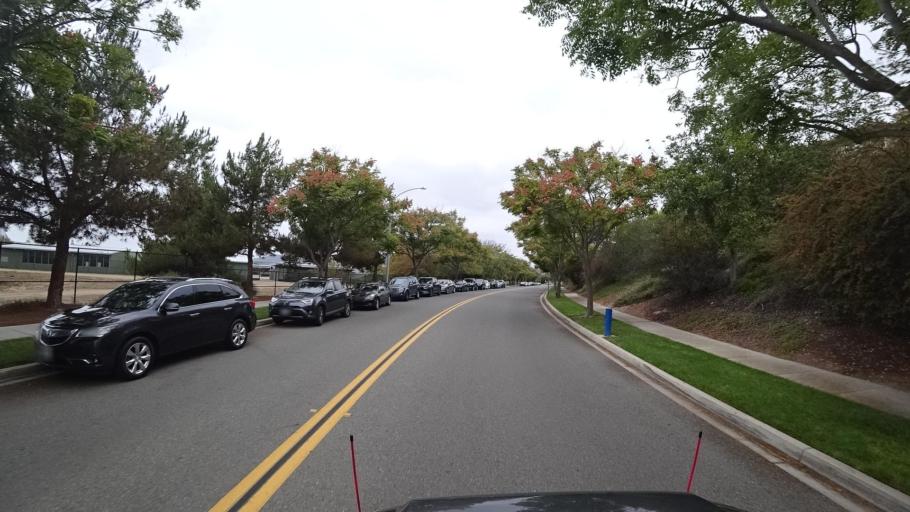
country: US
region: California
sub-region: San Diego County
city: Fairbanks Ranch
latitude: 33.0128
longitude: -117.1198
